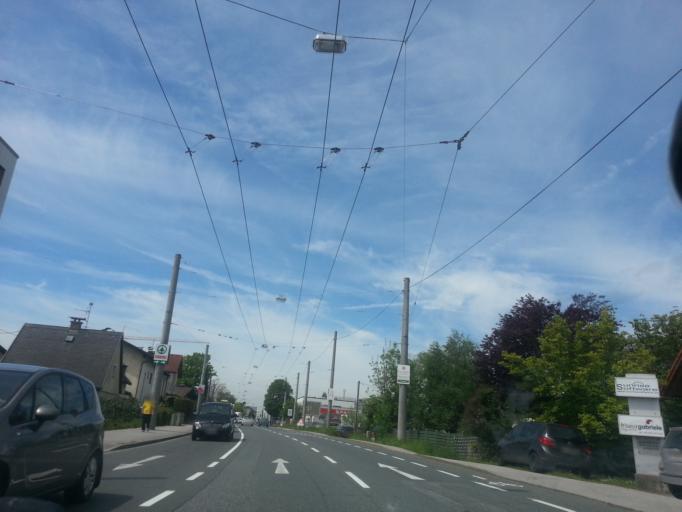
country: AT
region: Salzburg
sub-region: Politischer Bezirk Salzburg-Umgebung
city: Bergheim
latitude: 47.8280
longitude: 13.0090
